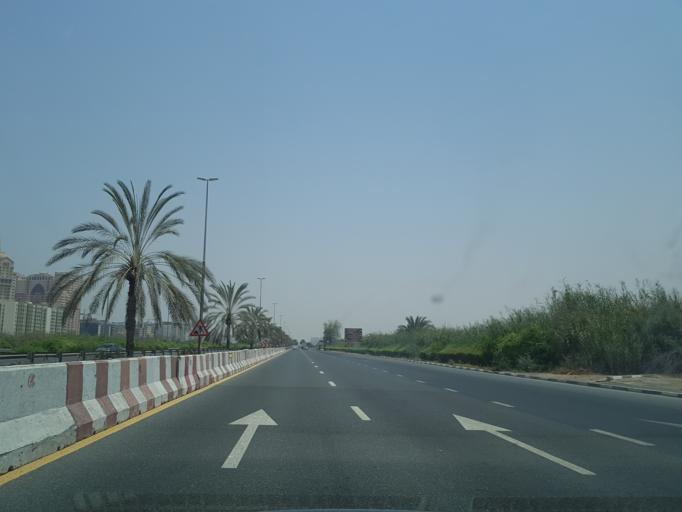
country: AE
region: Dubai
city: Dubai
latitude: 25.1098
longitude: 55.3877
